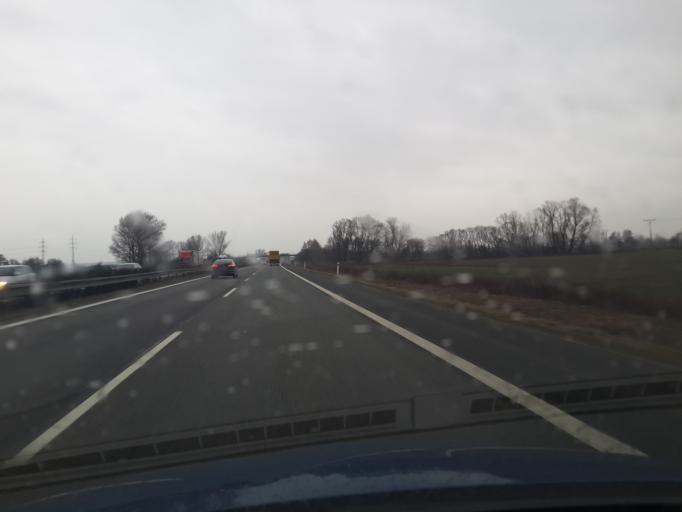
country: SK
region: Bratislavsky
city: Stupava
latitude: 48.2312
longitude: 17.0217
